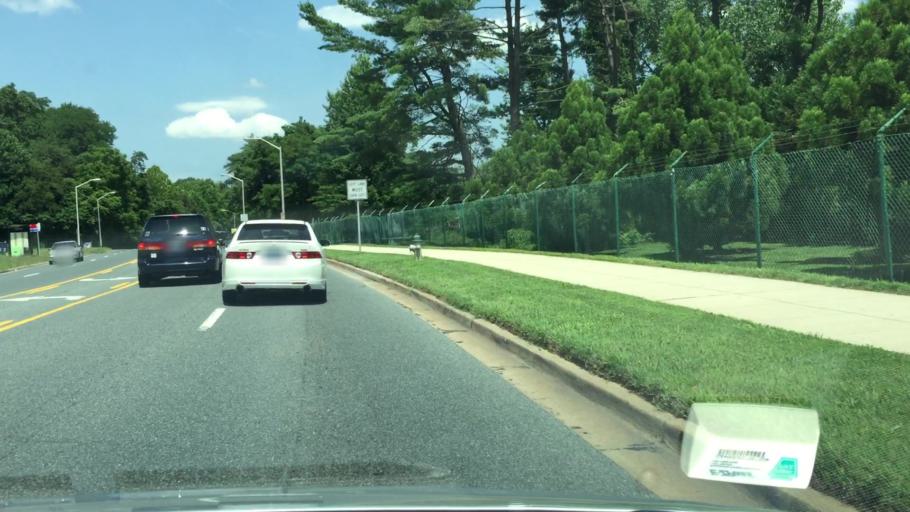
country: US
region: Maryland
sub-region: Montgomery County
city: Aspen Hill
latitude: 39.0856
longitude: -77.0745
